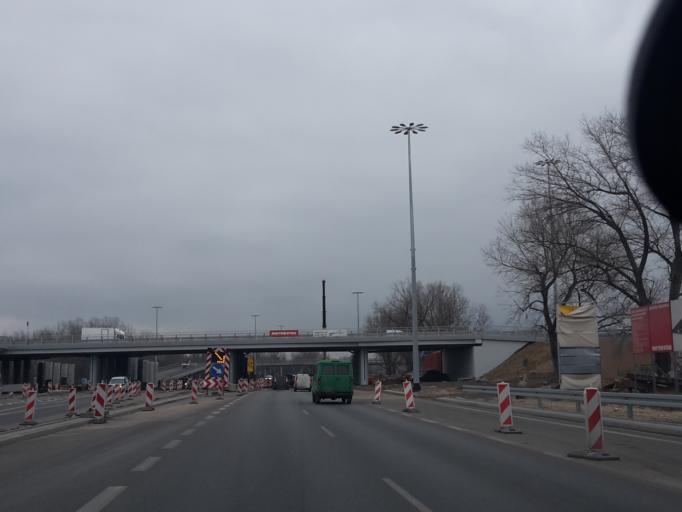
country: PL
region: Masovian Voivodeship
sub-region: Warszawa
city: Zoliborz
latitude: 52.2852
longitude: 20.9871
